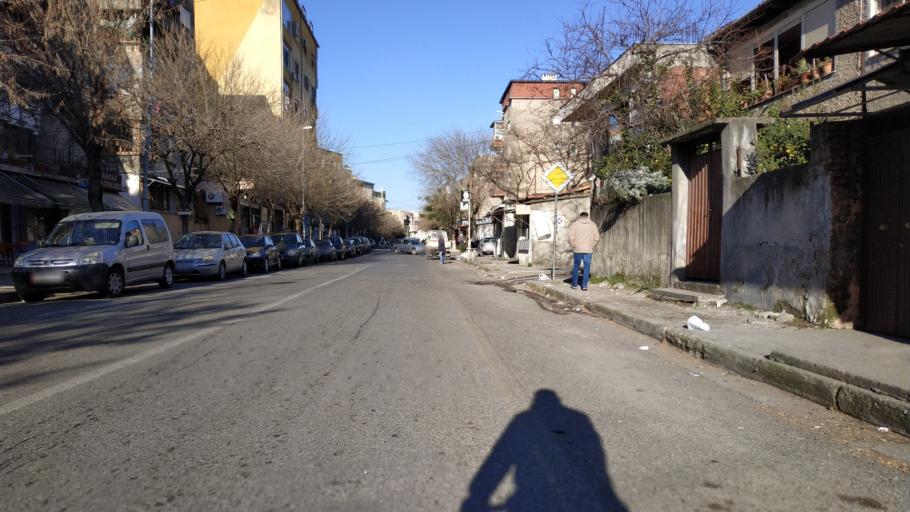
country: AL
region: Shkoder
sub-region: Rrethi i Shkodres
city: Shkoder
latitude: 42.0630
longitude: 19.5107
